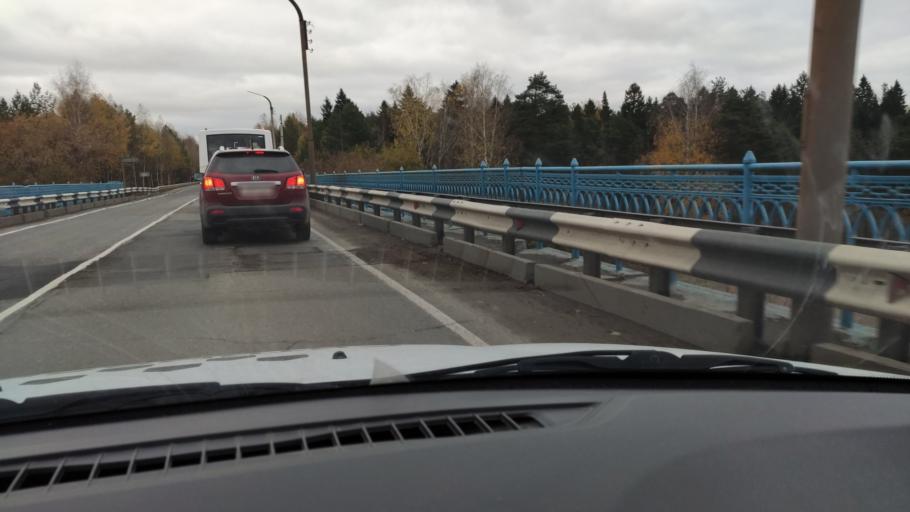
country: RU
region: Kirov
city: Slobodskoy
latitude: 58.7251
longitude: 50.1949
